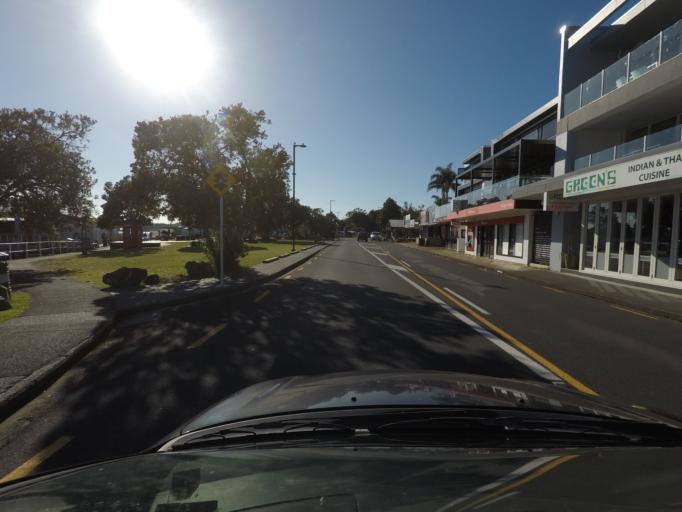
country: NZ
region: Northland
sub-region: Far North District
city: Paihia
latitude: -35.2809
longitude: 174.0914
